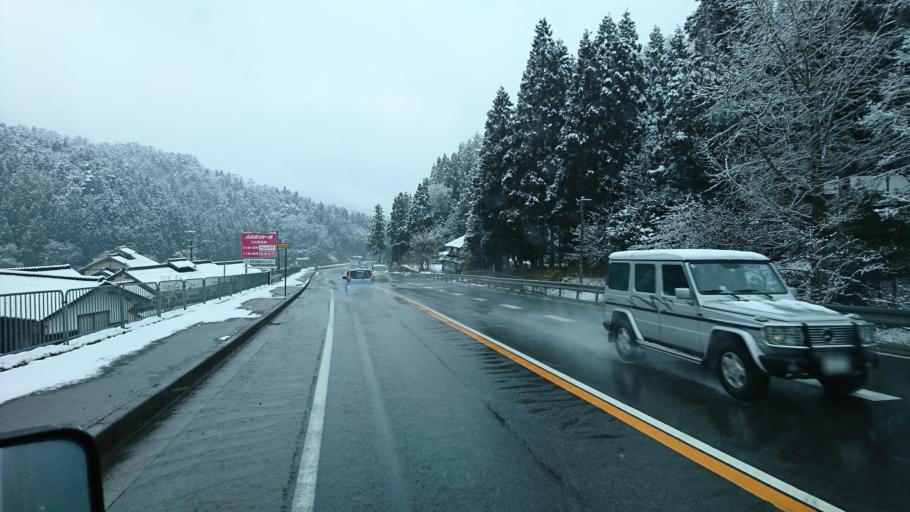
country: JP
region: Hyogo
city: Toyooka
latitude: 35.4071
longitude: 134.6042
